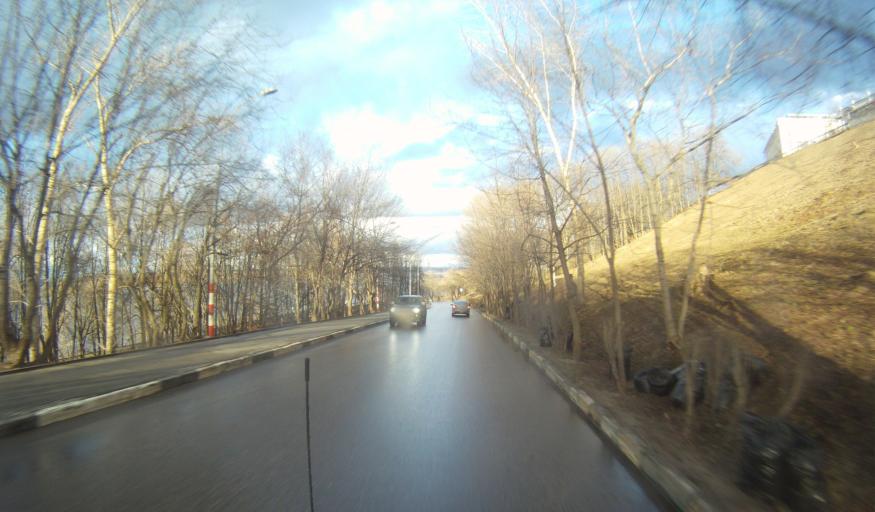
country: RU
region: Nizjnij Novgorod
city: Nizhniy Novgorod
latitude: 56.3302
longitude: 44.0151
